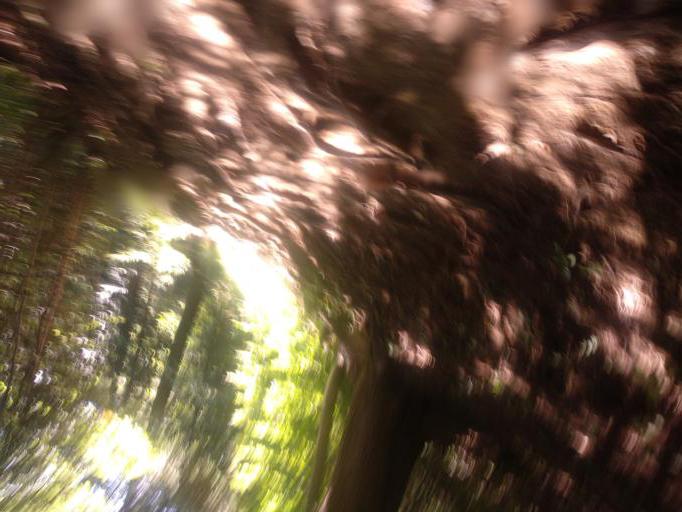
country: FR
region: Rhone-Alpes
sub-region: Departement de l'Isere
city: Le Sappey-en-Chartreuse
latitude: 45.2873
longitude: 5.7778
